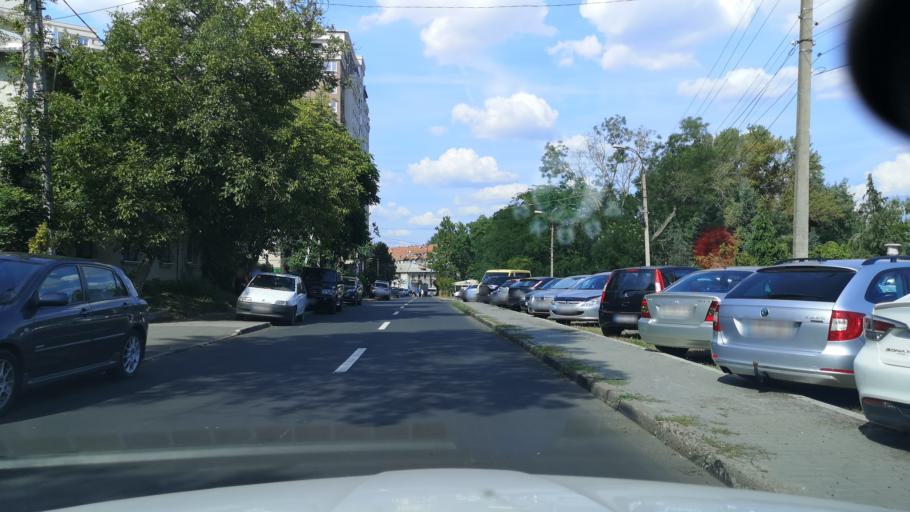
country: MD
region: Chisinau
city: Chisinau
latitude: 47.0315
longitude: 28.8074
